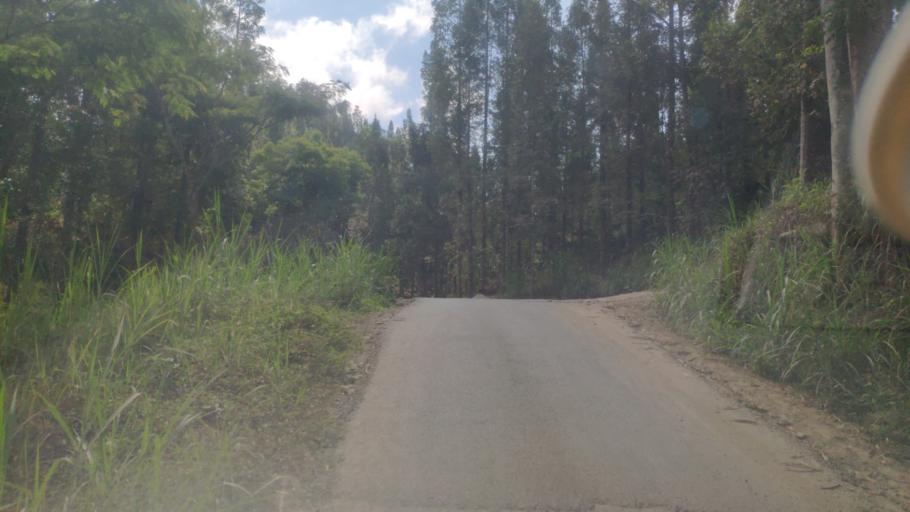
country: ID
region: Central Java
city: Wonosobo
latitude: -7.4453
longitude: 109.7099
